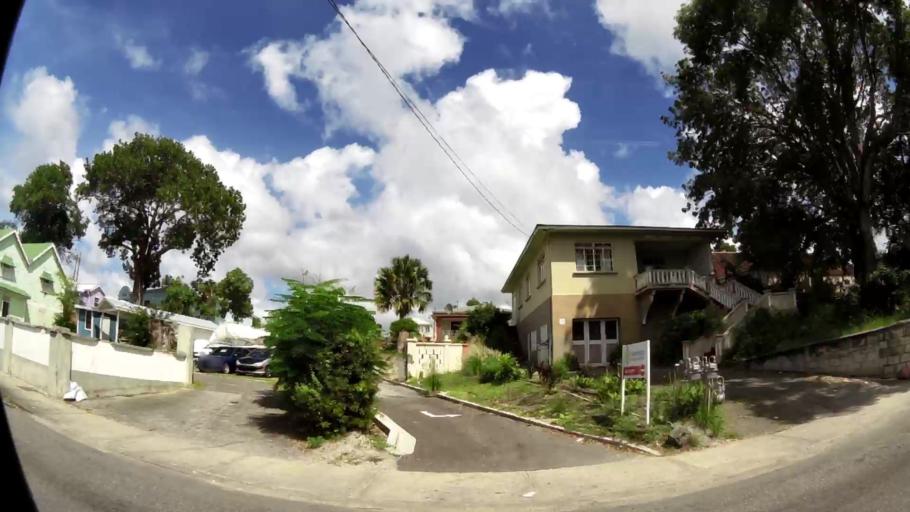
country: BB
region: Saint Michael
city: Bridgetown
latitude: 13.1265
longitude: -59.6272
